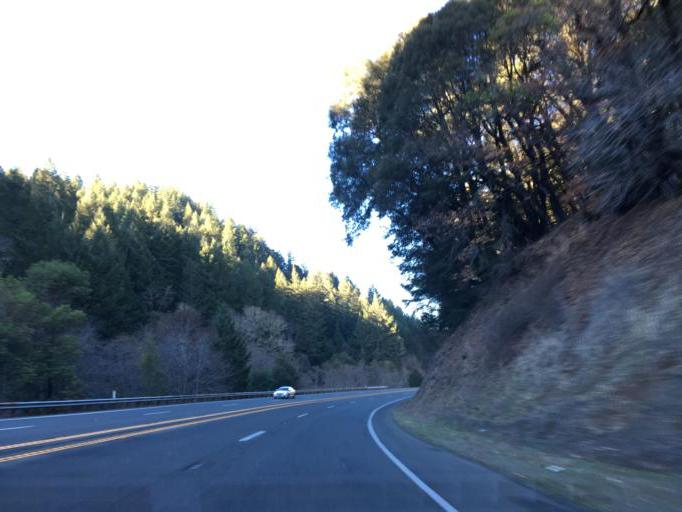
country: US
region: California
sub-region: Mendocino County
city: Laytonville
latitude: 39.5720
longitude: -123.4375
